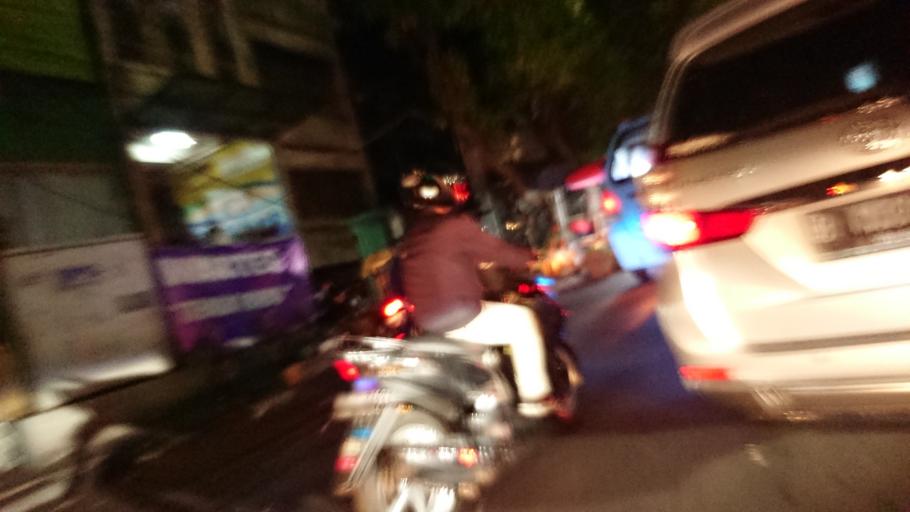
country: ID
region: Jakarta Raya
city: Jakarta
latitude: -6.1884
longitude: 106.8155
